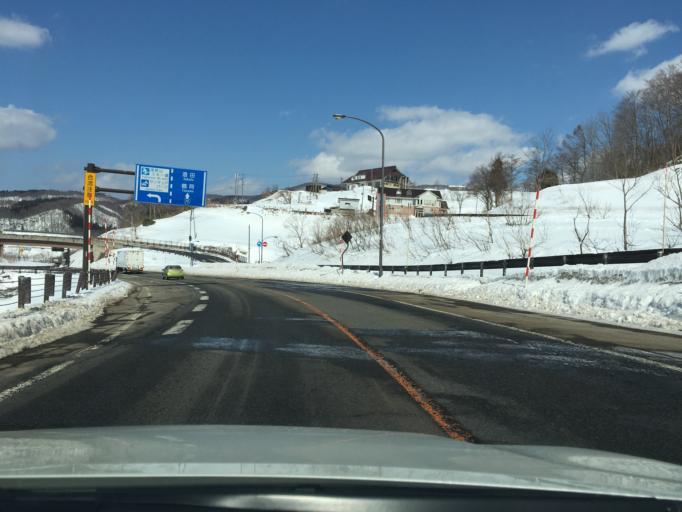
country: JP
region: Yamagata
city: Tsuruoka
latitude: 38.5699
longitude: 139.9381
